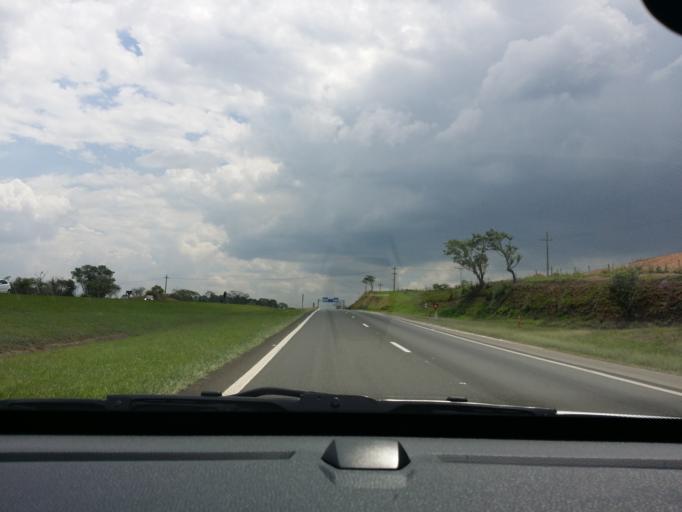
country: BR
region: Sao Paulo
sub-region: Rio Claro
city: Rio Claro
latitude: -22.3839
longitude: -47.6095
